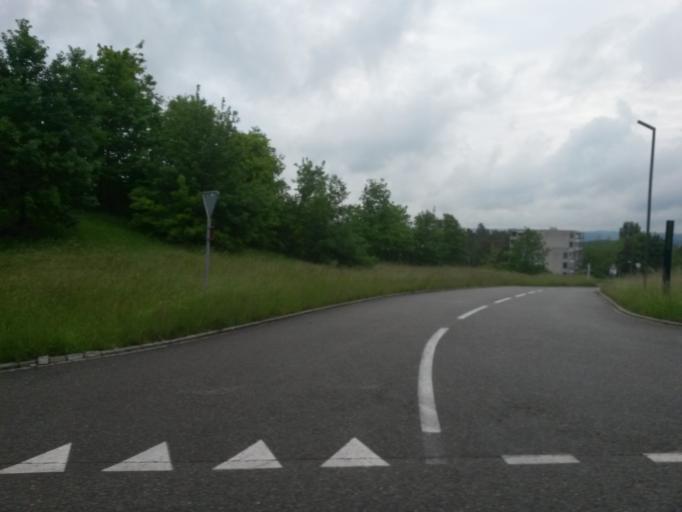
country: CH
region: Zurich
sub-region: Bezirk Zuerich
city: Zuerich (Kreis 10)
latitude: 47.4109
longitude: 8.5075
